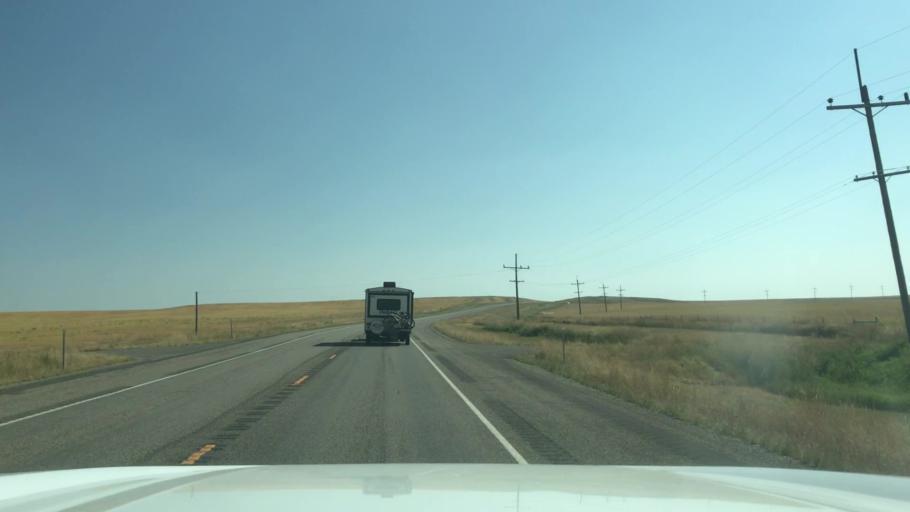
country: US
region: Montana
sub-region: Wheatland County
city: Harlowton
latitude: 46.4752
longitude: -109.7661
